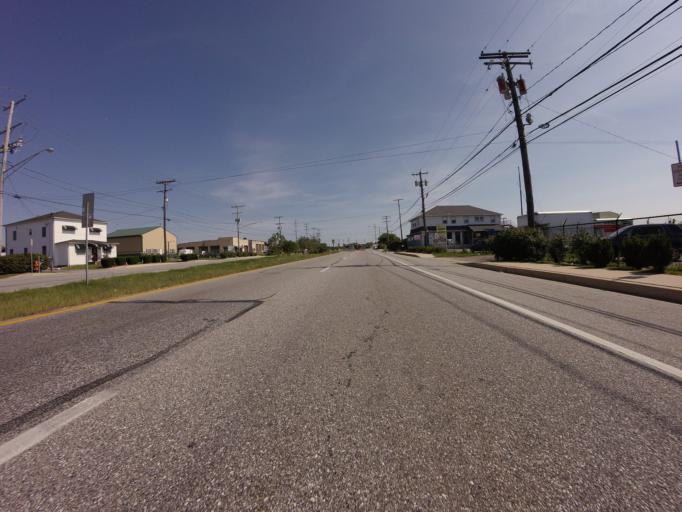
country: US
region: Maryland
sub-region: Baltimore County
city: Edgemere
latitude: 39.2556
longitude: -76.4618
